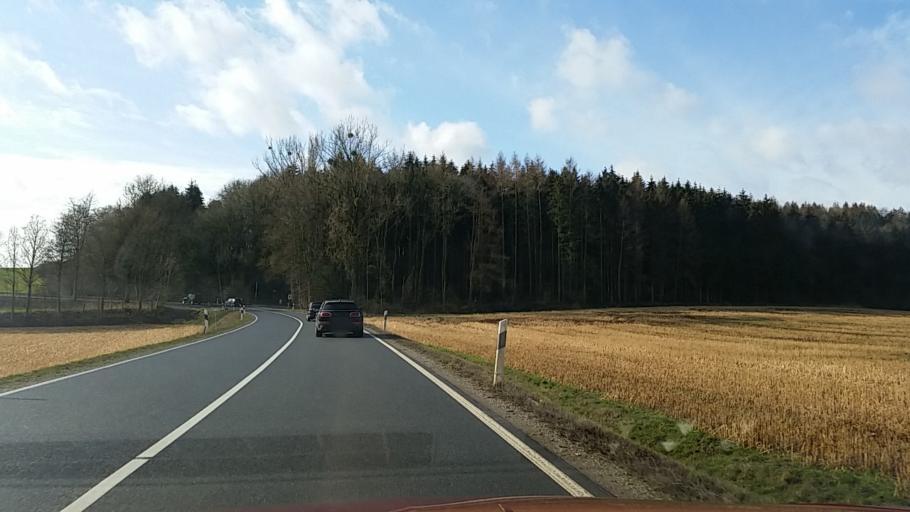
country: DE
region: Lower Saxony
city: Gittelde
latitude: 51.8358
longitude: 10.1135
